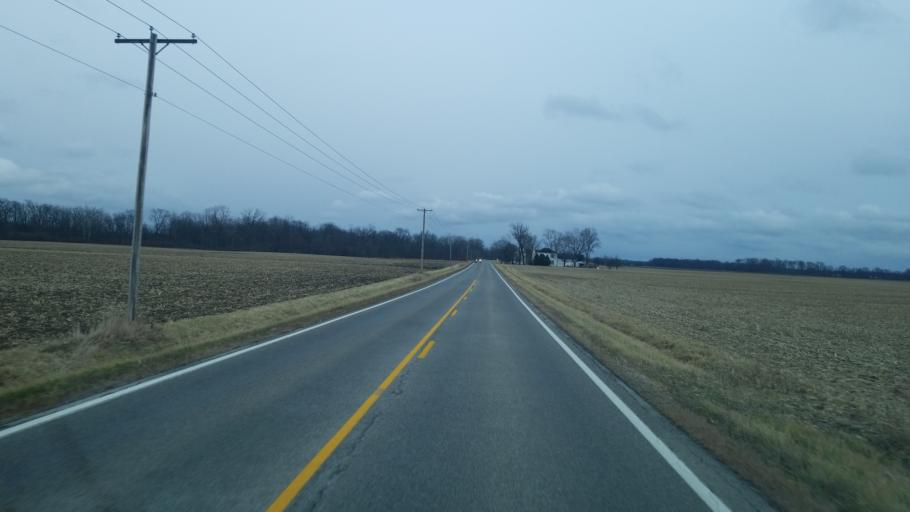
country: US
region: Ohio
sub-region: Union County
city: Richwood
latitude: 40.3370
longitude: -83.2263
